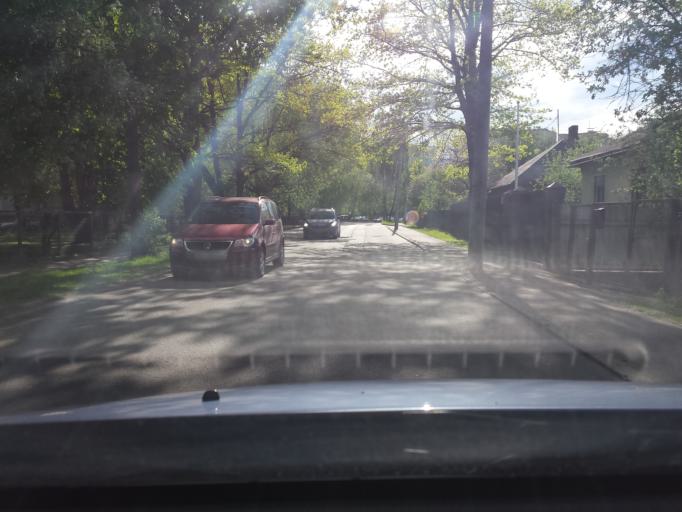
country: LV
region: Riga
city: Riga
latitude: 56.9534
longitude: 24.1778
